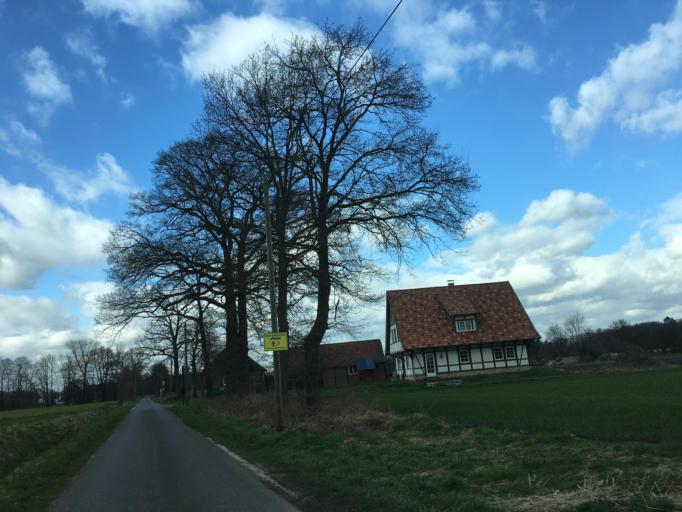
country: DE
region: North Rhine-Westphalia
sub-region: Regierungsbezirk Munster
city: Steinfurt
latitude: 52.1175
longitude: 7.3278
